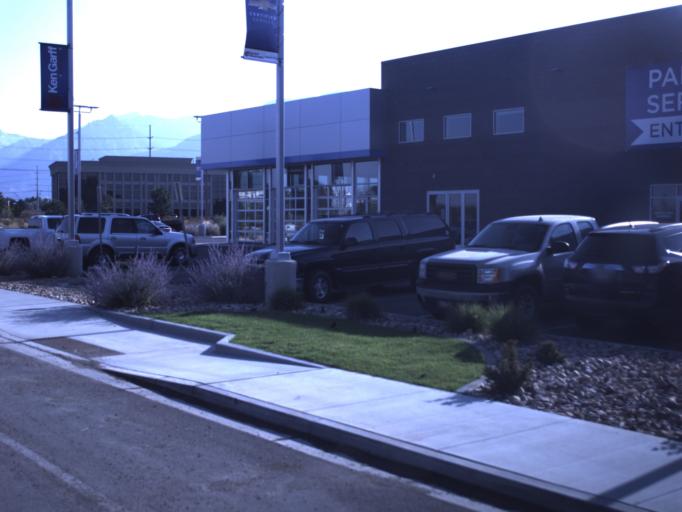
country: US
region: Utah
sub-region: Utah County
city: American Fork
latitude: 40.3564
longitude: -111.7855
